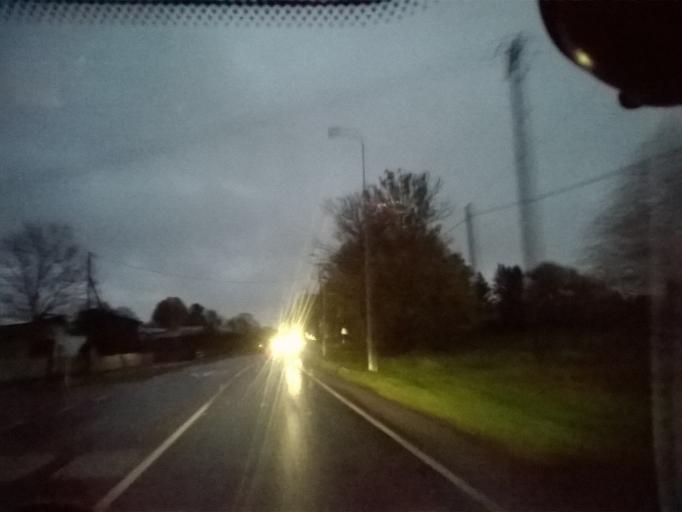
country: EE
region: Harju
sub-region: Viimsi vald
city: Viimsi
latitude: 59.5161
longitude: 24.8478
